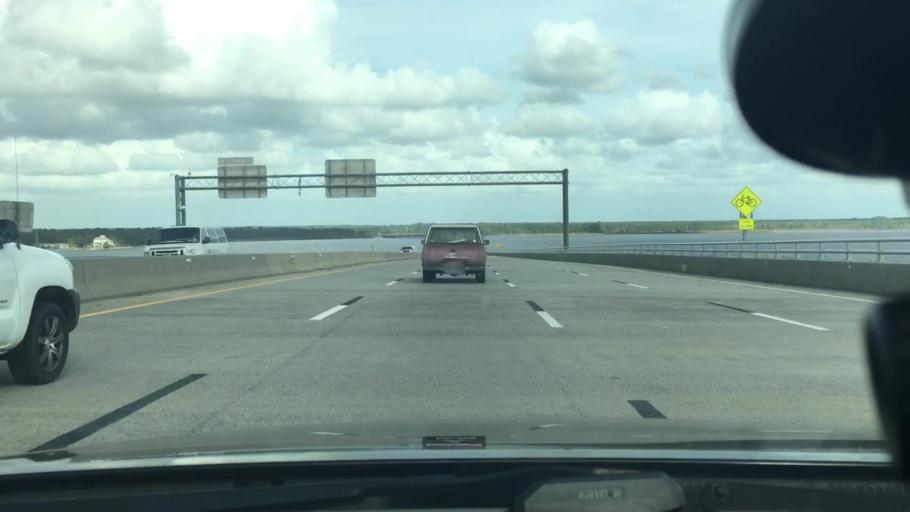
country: US
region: North Carolina
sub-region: Craven County
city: James City
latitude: 35.0965
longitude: -77.0287
